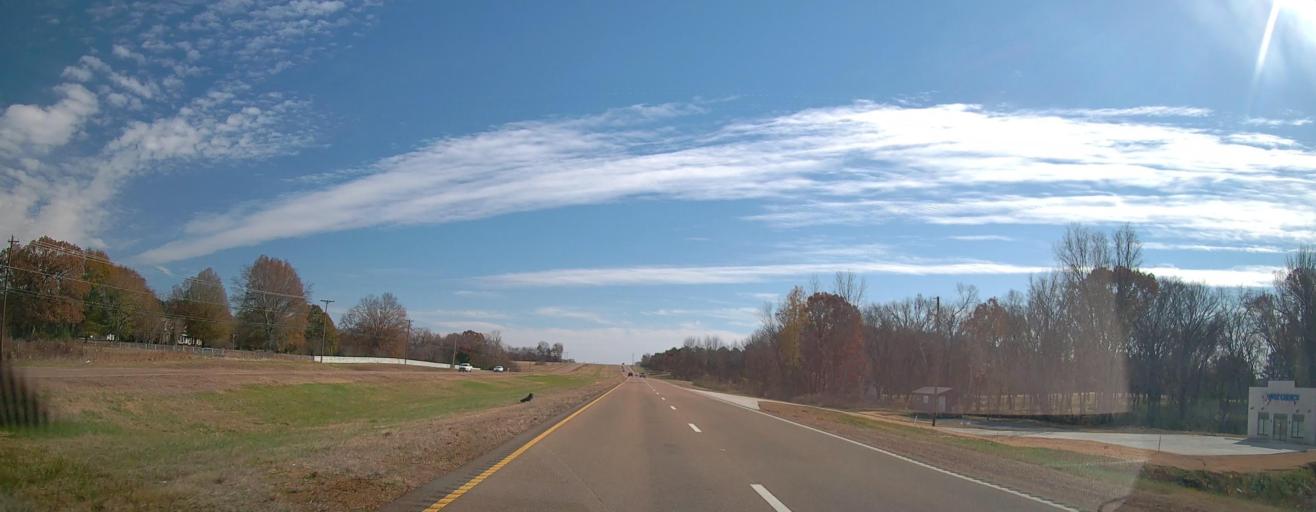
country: US
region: Tennessee
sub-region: Fayette County
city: Piperton
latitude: 34.9730
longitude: -89.5633
